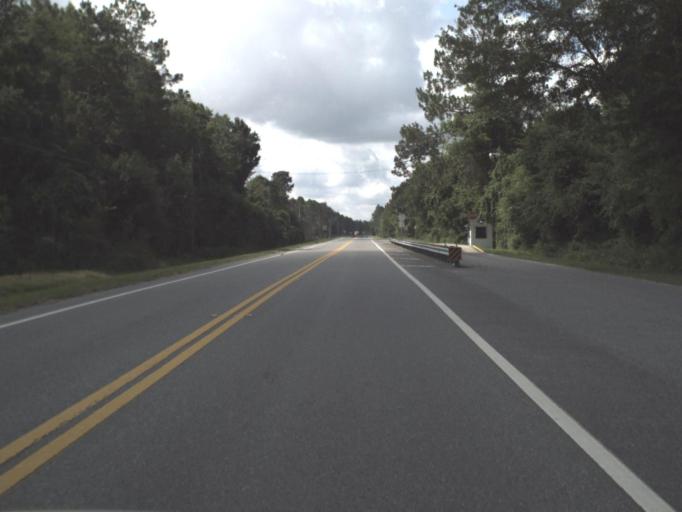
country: US
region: Florida
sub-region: Baker County
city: Macclenny
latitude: 30.3250
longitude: -82.1250
